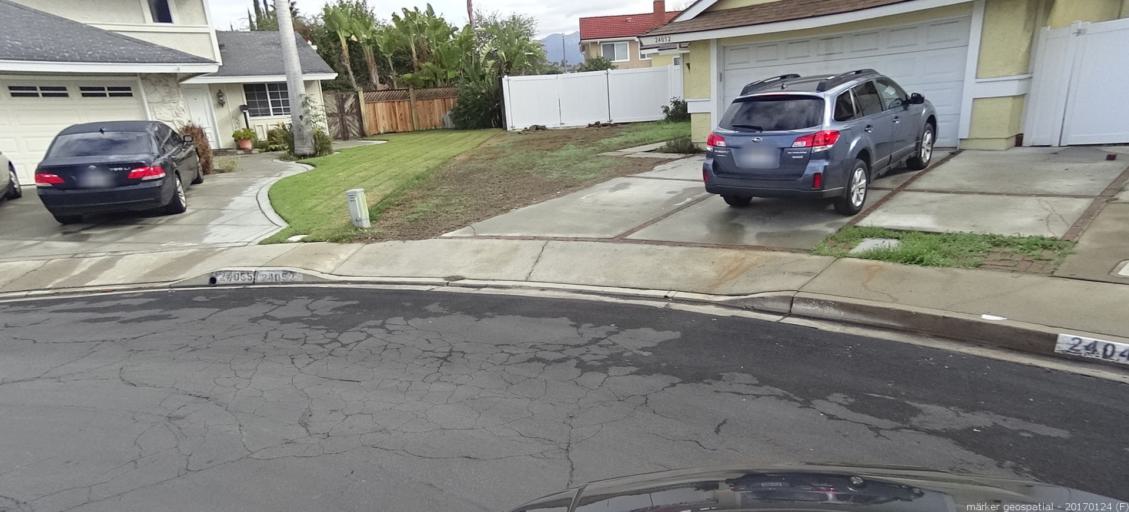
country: US
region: California
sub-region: Orange County
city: Laguna Hills
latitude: 33.6265
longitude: -117.7106
